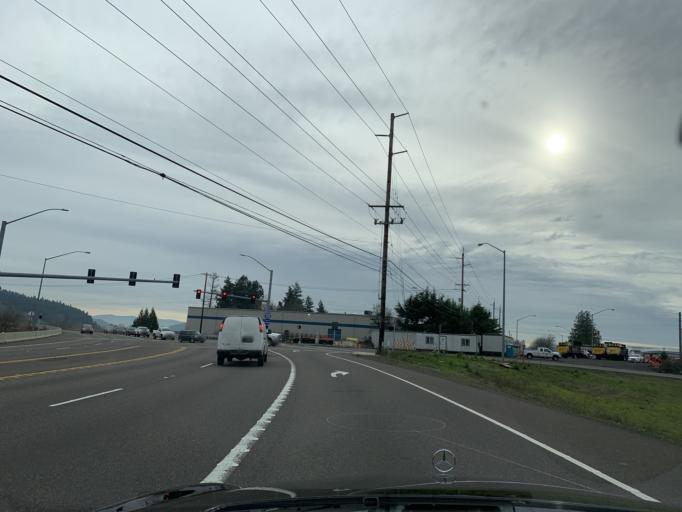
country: US
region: Oregon
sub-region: Clackamas County
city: Clackamas
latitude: 45.4192
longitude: -122.5720
